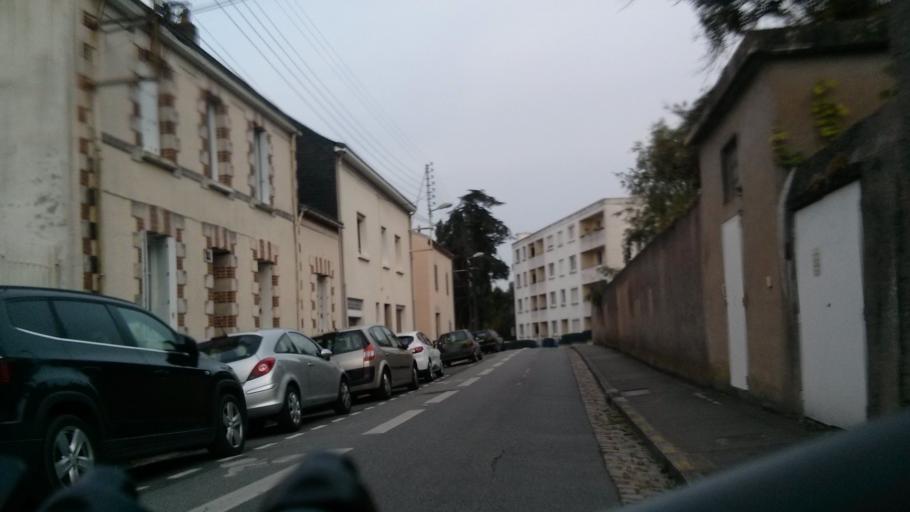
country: FR
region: Pays de la Loire
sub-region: Departement de la Loire-Atlantique
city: Reze
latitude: 47.1928
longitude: -1.5361
